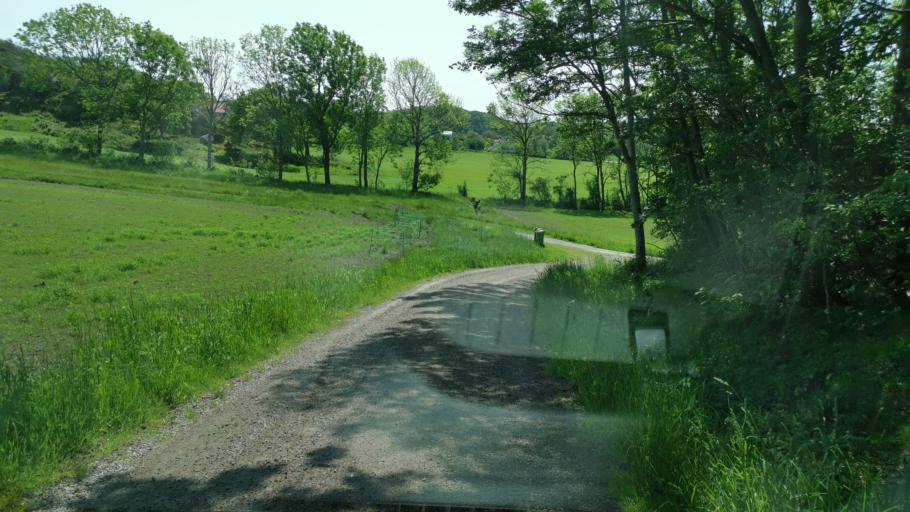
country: SE
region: Vaestra Goetaland
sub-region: Lysekils Kommun
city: Brastad
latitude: 58.3003
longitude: 11.5403
